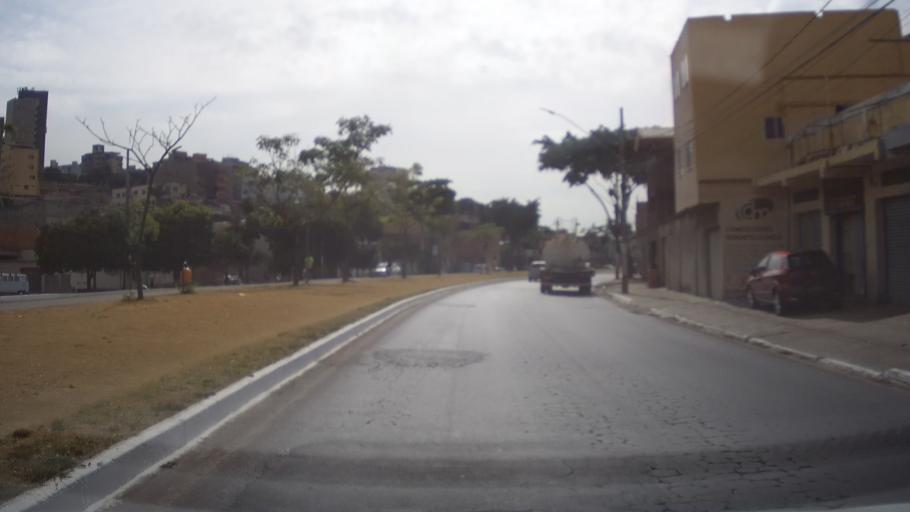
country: BR
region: Minas Gerais
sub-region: Contagem
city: Contagem
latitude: -19.9483
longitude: -44.0427
